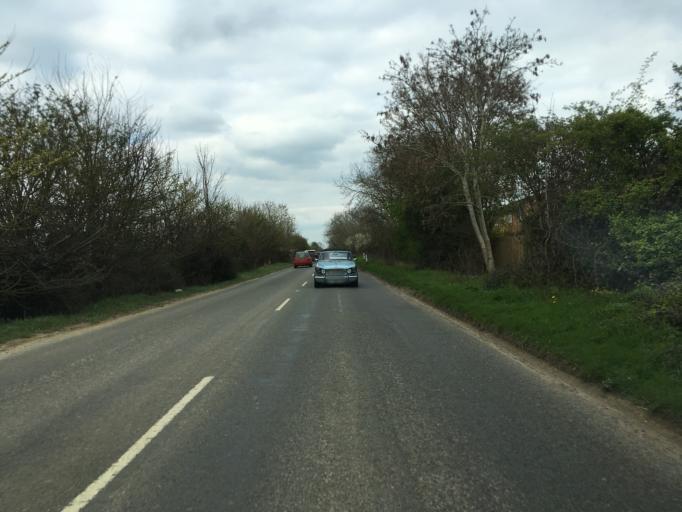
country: GB
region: England
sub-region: Oxfordshire
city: Bicester
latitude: 51.9020
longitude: -1.1805
